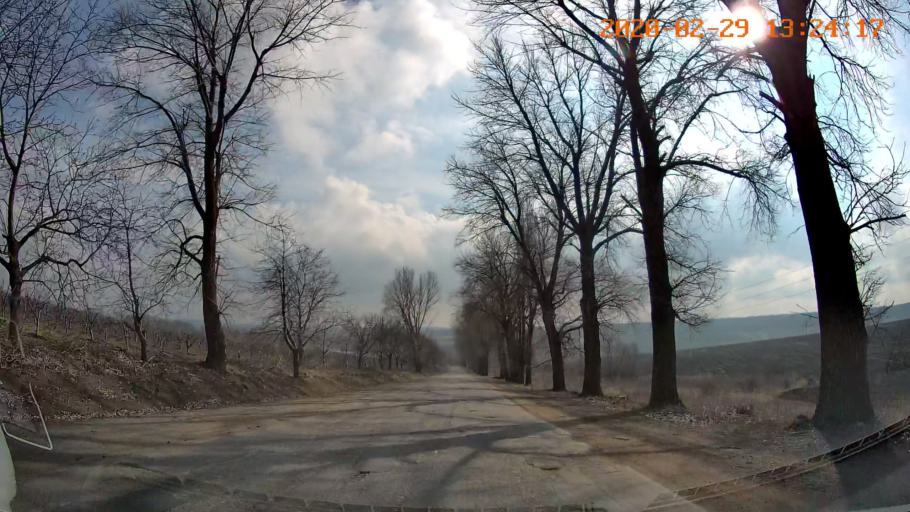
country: MD
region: Telenesti
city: Camenca
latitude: 47.9405
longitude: 28.6267
